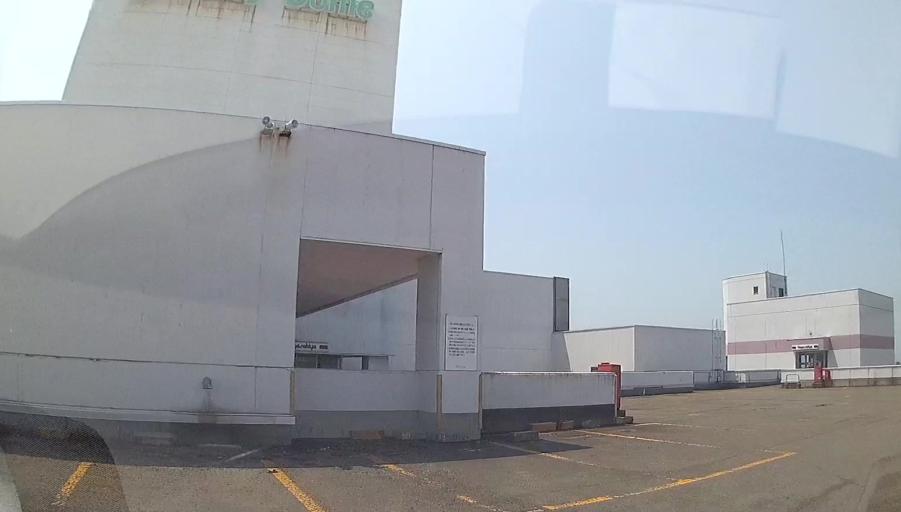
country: JP
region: Hokkaido
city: Obihiro
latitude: 42.9182
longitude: 143.1993
